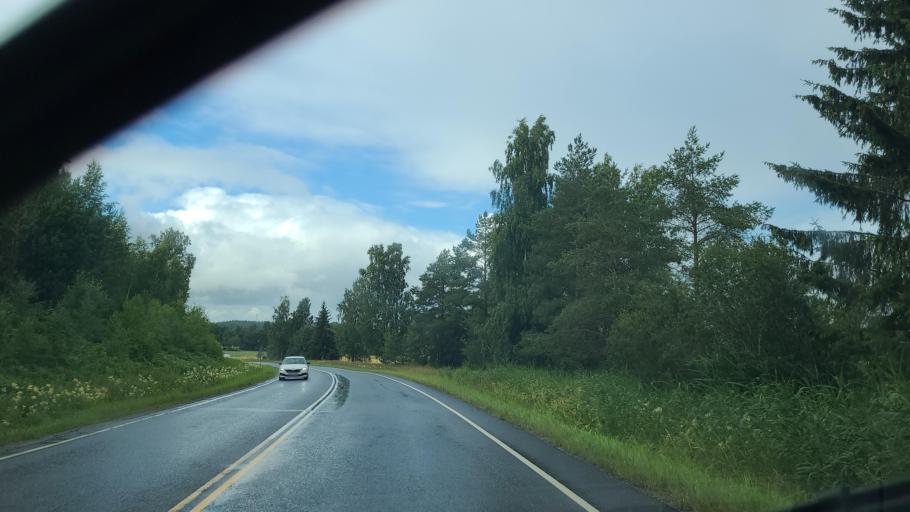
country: FI
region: Varsinais-Suomi
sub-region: Turku
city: Sauvo
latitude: 60.3377
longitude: 22.7022
